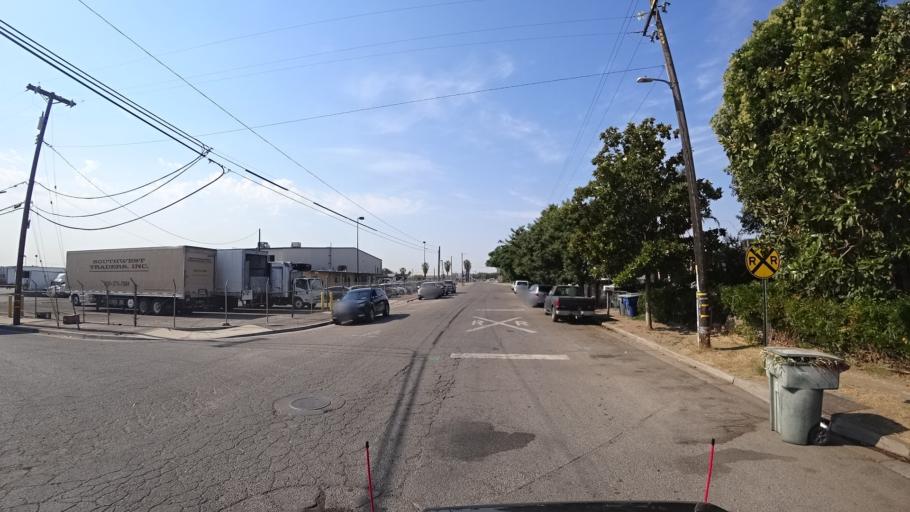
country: US
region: California
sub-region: Fresno County
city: Fresno
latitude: 36.7477
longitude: -119.8176
